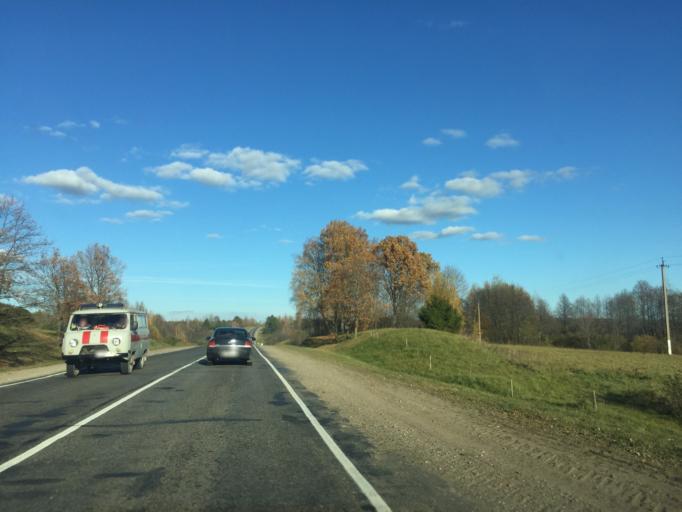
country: BY
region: Vitebsk
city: Dzisna
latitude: 55.2604
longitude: 28.1235
